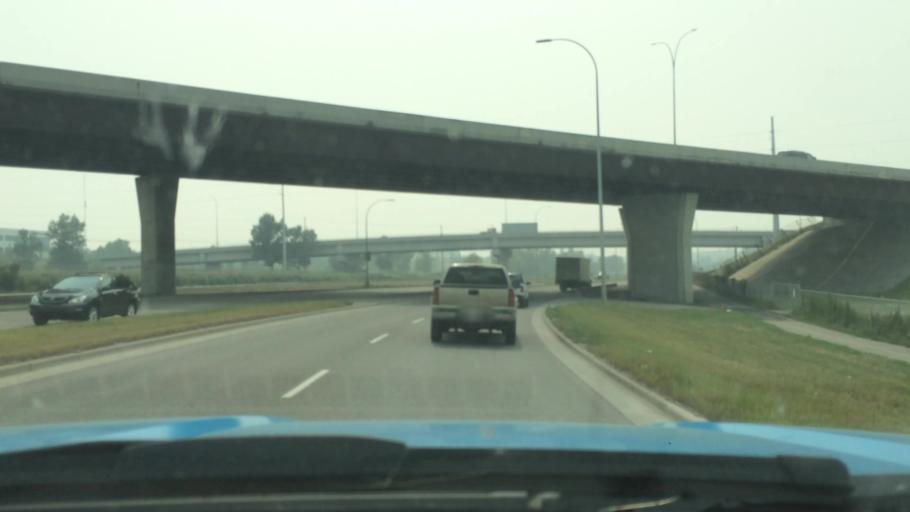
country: CA
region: Alberta
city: Calgary
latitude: 51.0108
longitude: -114.0108
